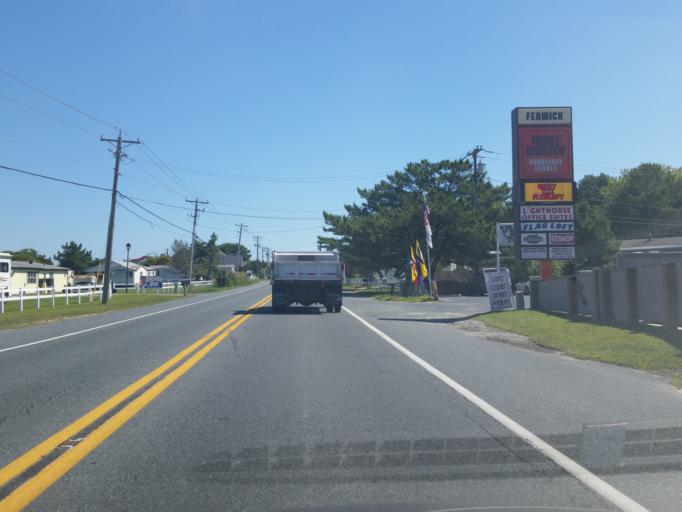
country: US
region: Delaware
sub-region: Sussex County
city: Bethany Beach
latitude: 38.4521
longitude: -75.0582
